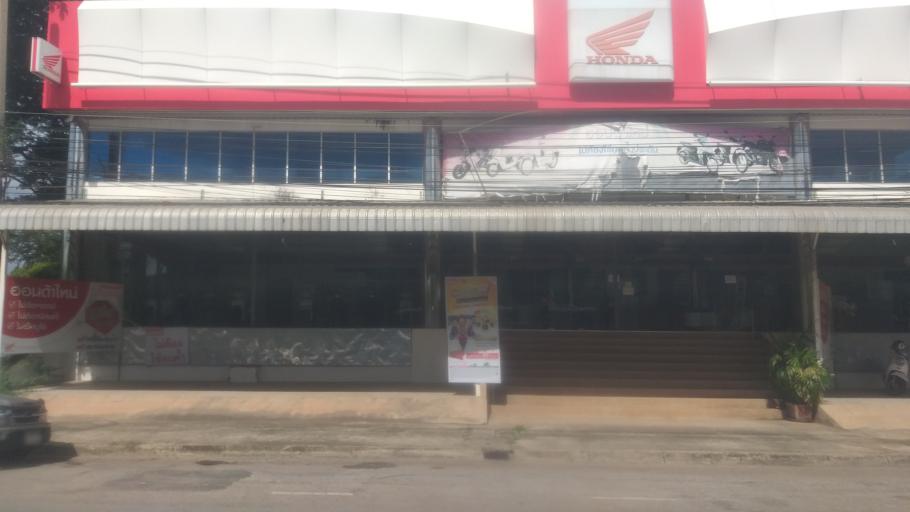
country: TH
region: Chaiyaphum
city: Chaiyaphum
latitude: 15.8005
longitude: 102.0311
